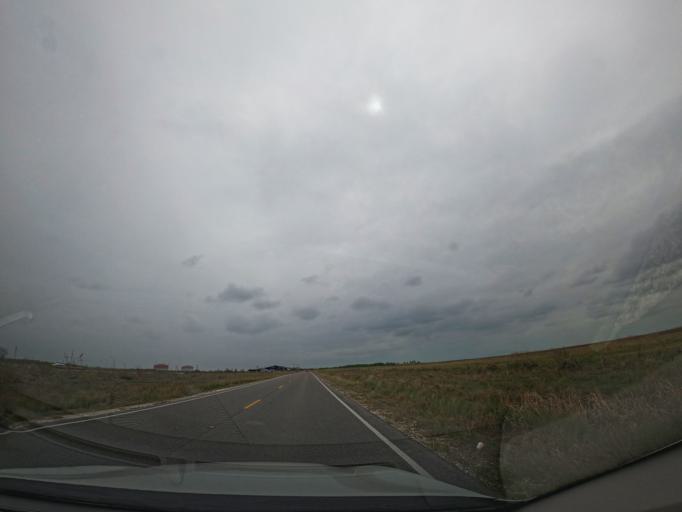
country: US
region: Louisiana
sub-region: Cameron Parish
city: Cameron
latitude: 29.7911
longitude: -93.3494
